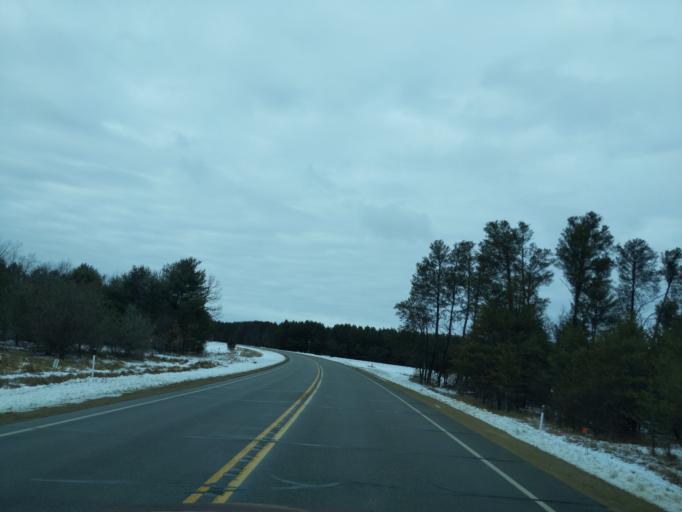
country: US
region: Wisconsin
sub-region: Waushara County
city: Wautoma
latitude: 43.9569
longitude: -89.3178
